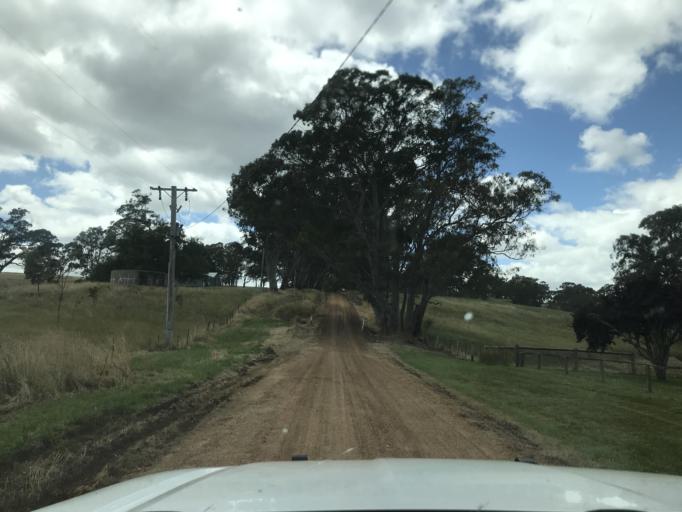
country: AU
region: South Australia
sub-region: Wattle Range
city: Penola
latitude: -37.3657
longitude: 141.2455
